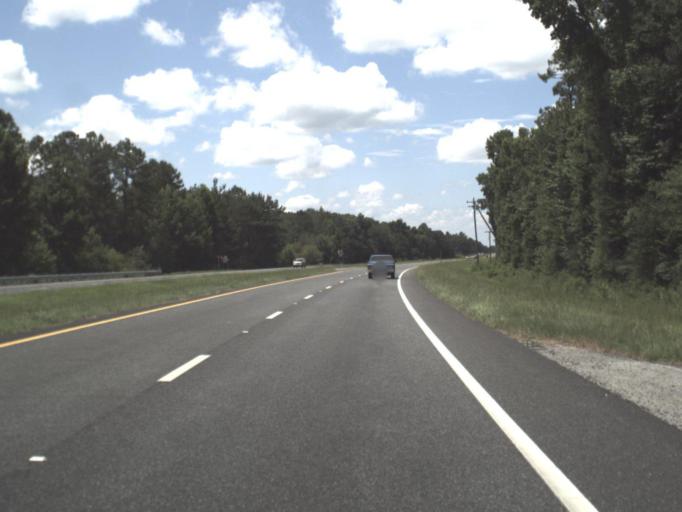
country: US
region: Florida
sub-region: Jefferson County
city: Monticello
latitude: 30.3476
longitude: -83.7917
